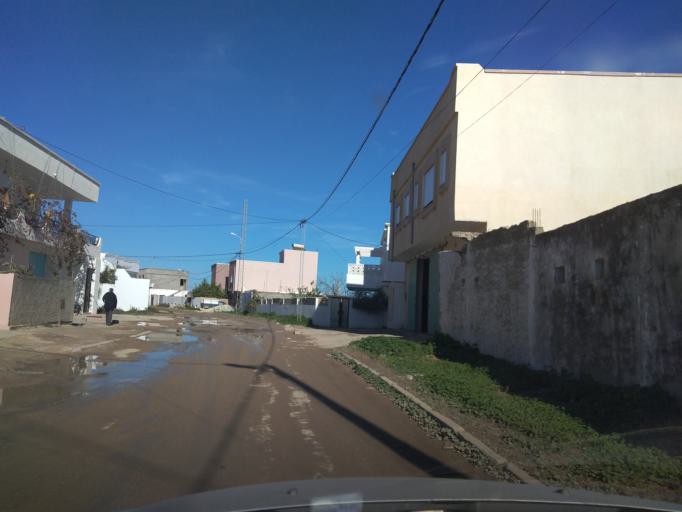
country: TN
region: Ariana
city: Qal'at al Andalus
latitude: 37.0631
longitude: 10.1247
